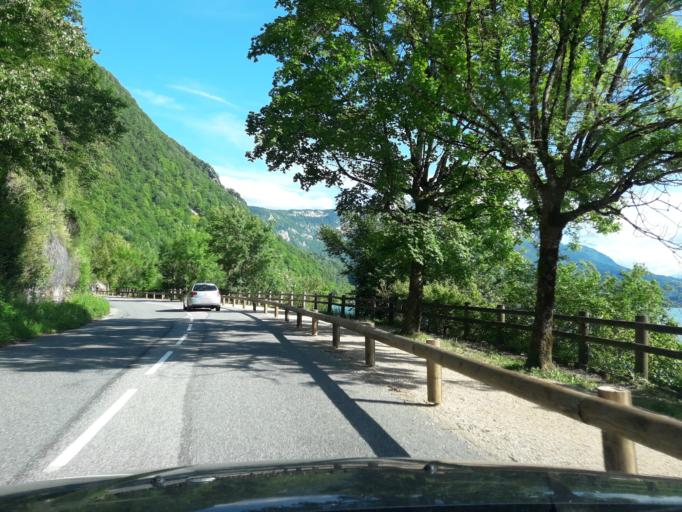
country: FR
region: Rhone-Alpes
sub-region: Departement de la Savoie
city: Novalaise
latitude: 45.5736
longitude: 5.8063
